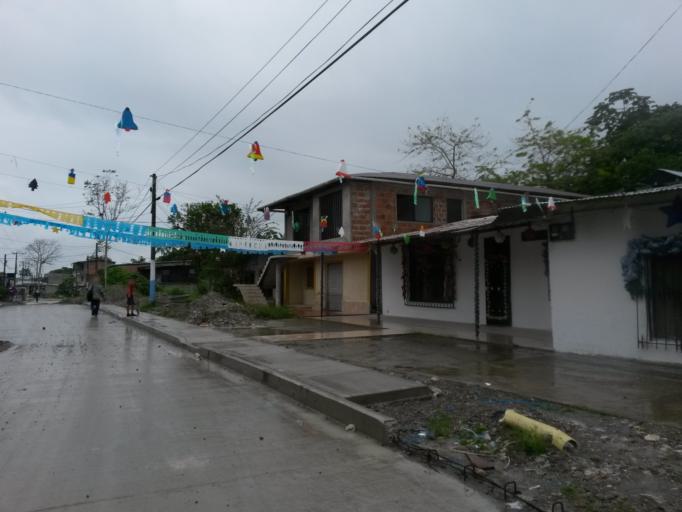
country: CO
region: Cauca
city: Guapi
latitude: 2.5725
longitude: -77.8895
